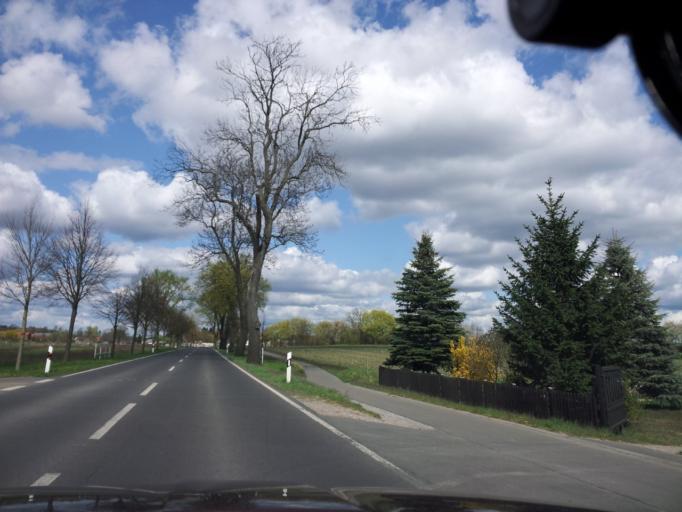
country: DE
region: Brandenburg
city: Rudnitz
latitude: 52.7143
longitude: 13.6196
